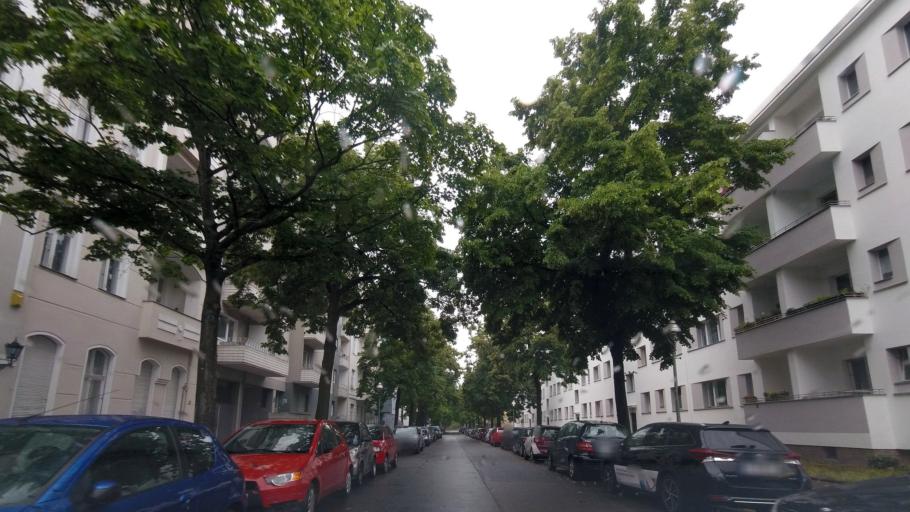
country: DE
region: Berlin
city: Wilmersdorf Bezirk
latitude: 52.4862
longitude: 13.3158
